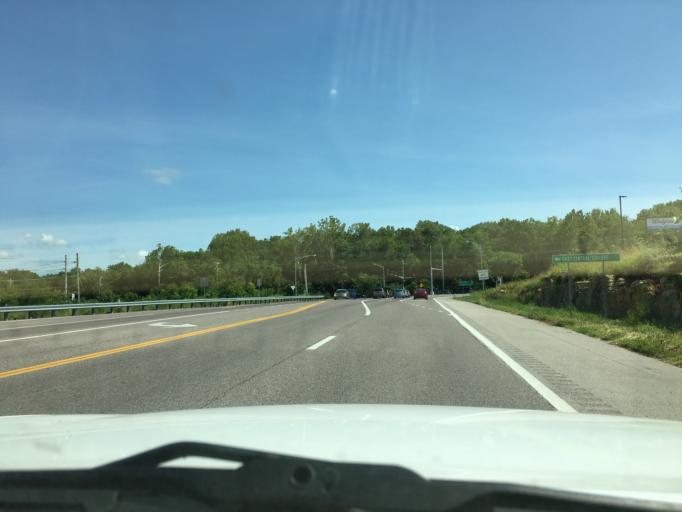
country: US
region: Missouri
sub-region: Franklin County
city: Union
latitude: 38.4456
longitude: -90.9983
